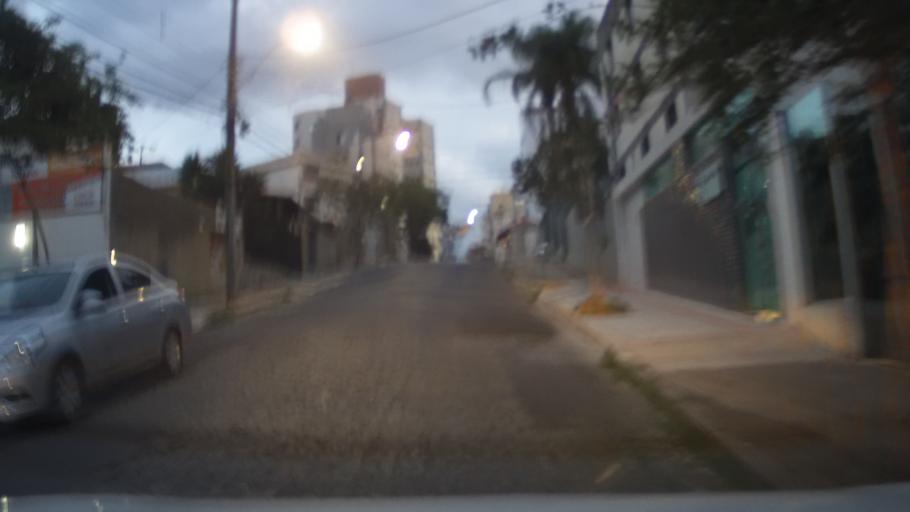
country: BR
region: Minas Gerais
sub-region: Belo Horizonte
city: Belo Horizonte
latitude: -19.8952
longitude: -43.9334
